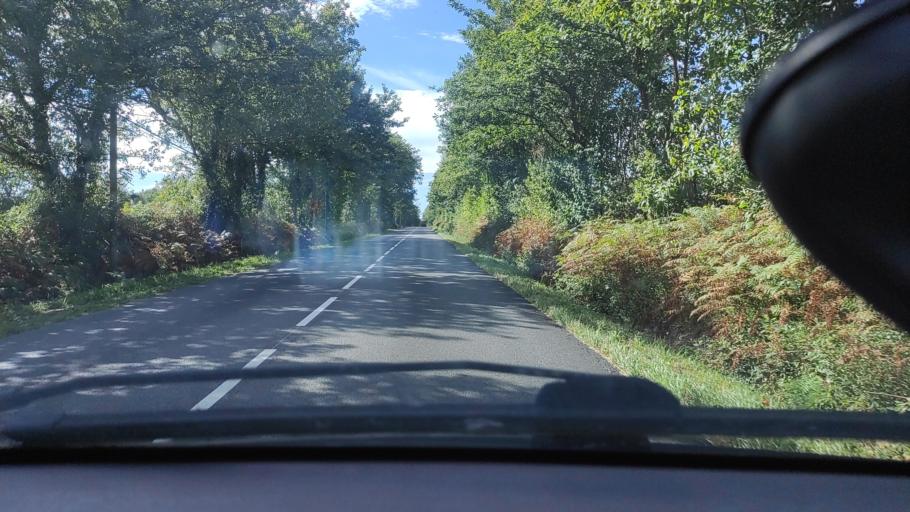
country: FR
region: Pays de la Loire
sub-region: Departement de la Vendee
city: La Boissiere-des-Landes
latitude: 46.5505
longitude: -1.4205
